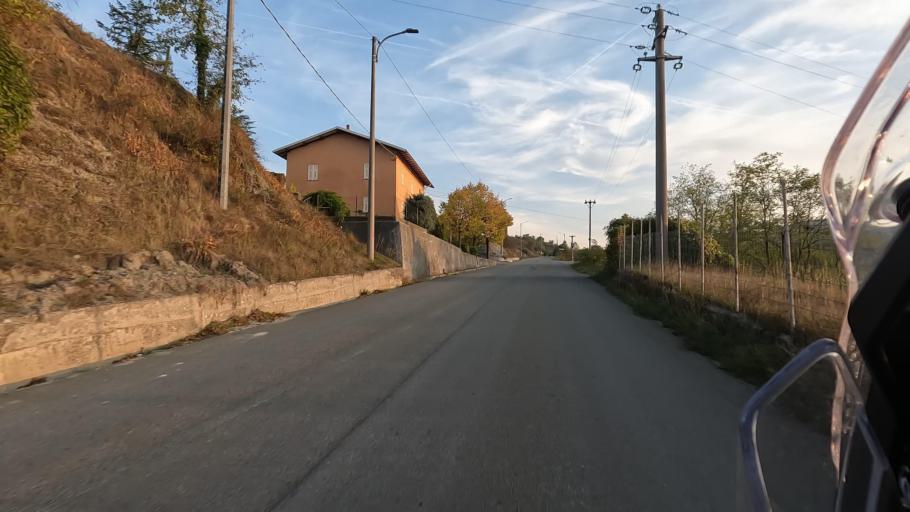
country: IT
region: Liguria
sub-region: Provincia di Savona
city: Mioglia
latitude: 44.4847
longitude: 8.4128
